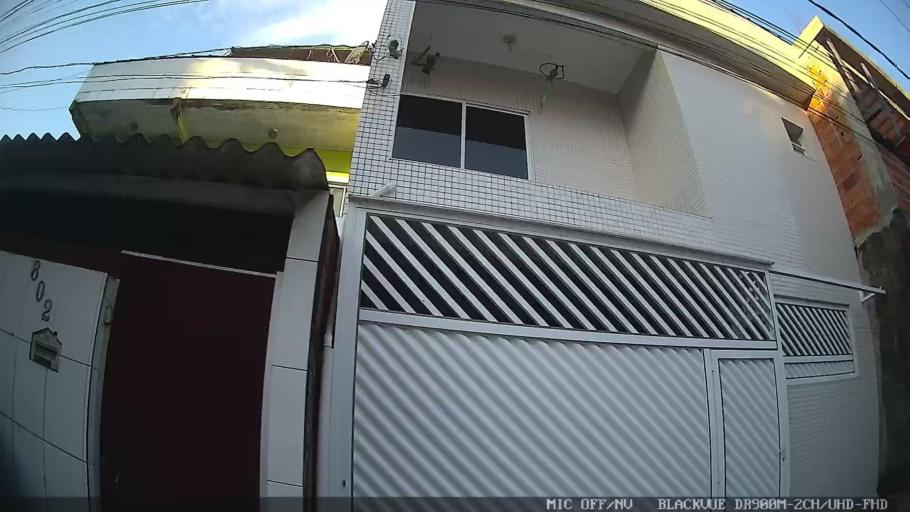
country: BR
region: Sao Paulo
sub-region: Guaruja
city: Guaruja
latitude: -23.9856
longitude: -46.2764
